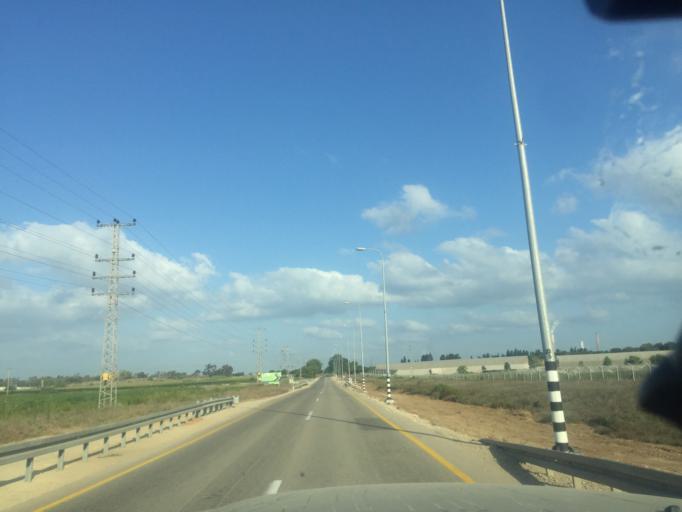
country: PS
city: Umm an Nasr
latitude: 31.6064
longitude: 34.5545
